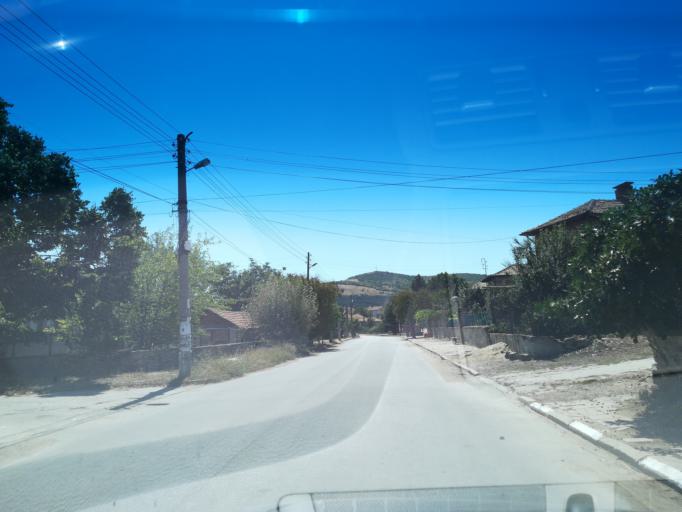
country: BG
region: Pazardzhik
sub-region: Obshtina Pazardzhik
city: Pazardzhik
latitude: 42.3366
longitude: 24.4012
